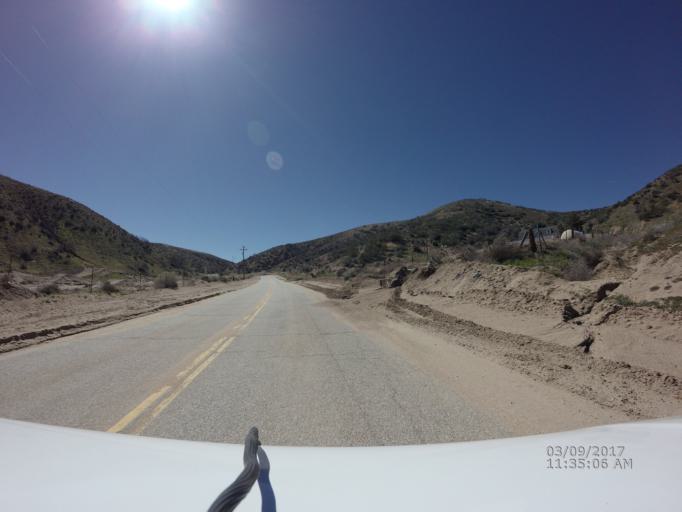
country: US
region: California
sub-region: Los Angeles County
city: Green Valley
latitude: 34.6812
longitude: -118.3922
